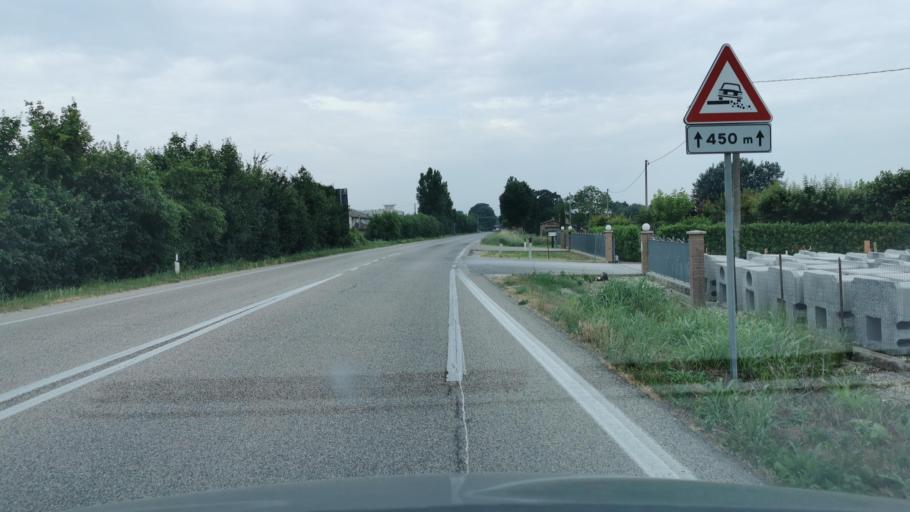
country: IT
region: Emilia-Romagna
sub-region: Provincia di Ravenna
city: Fornace Zarattini
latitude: 44.4122
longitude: 12.1259
